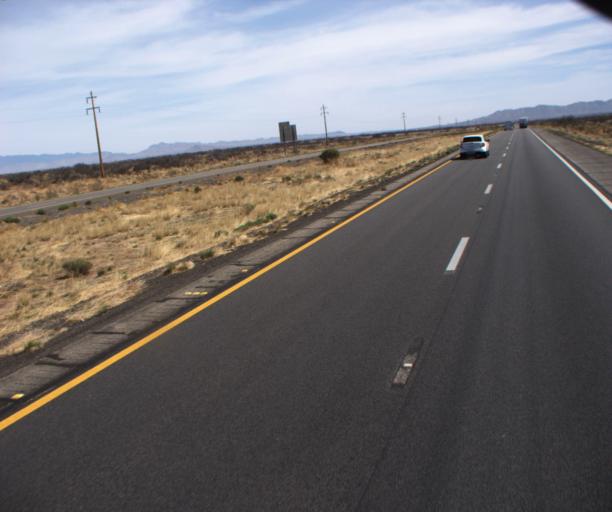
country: US
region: Arizona
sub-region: Cochise County
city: Willcox
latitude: 32.1871
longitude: -109.9313
